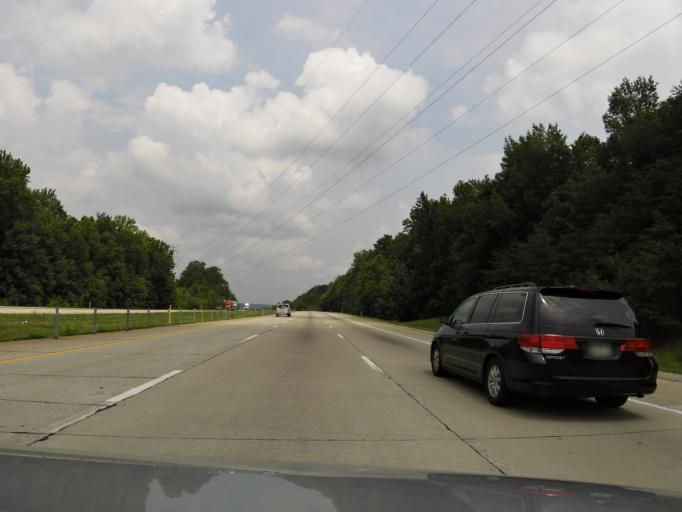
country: US
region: Kentucky
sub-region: Bullitt County
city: Lebanon Junction
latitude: 37.9074
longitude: -85.6910
